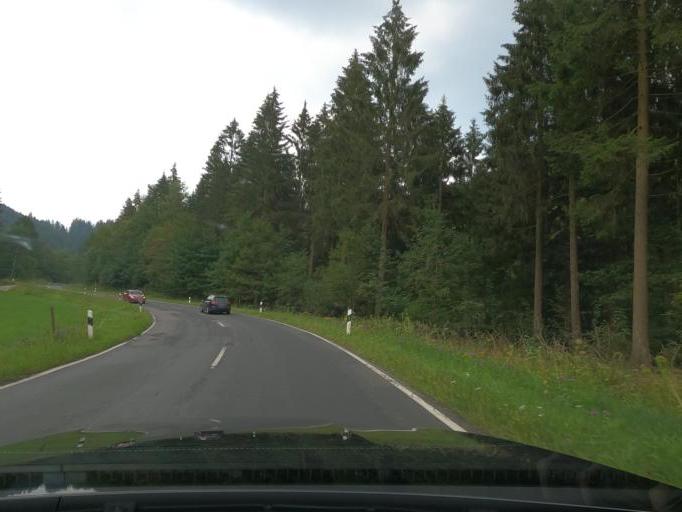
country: DE
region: Lower Saxony
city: Wildemann
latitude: 51.8353
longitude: 10.2669
